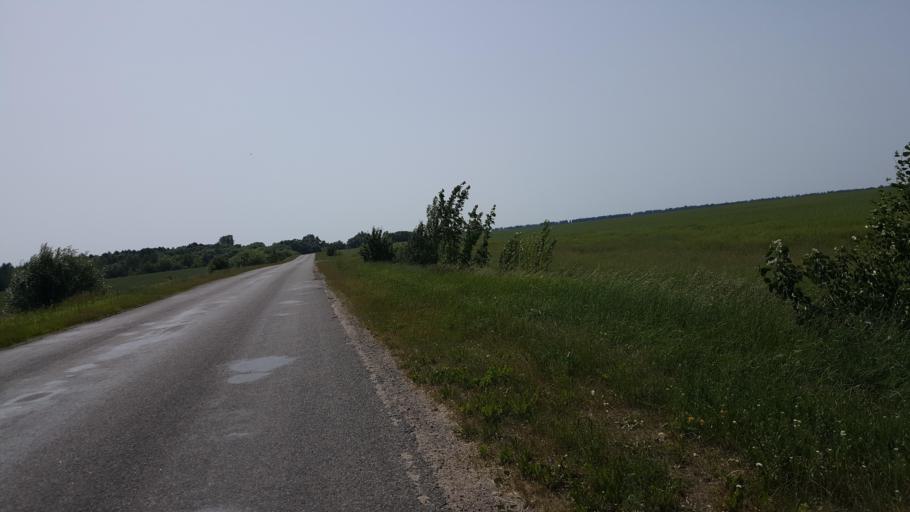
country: BY
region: Brest
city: Kamyanyets
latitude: 52.4325
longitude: 23.8285
